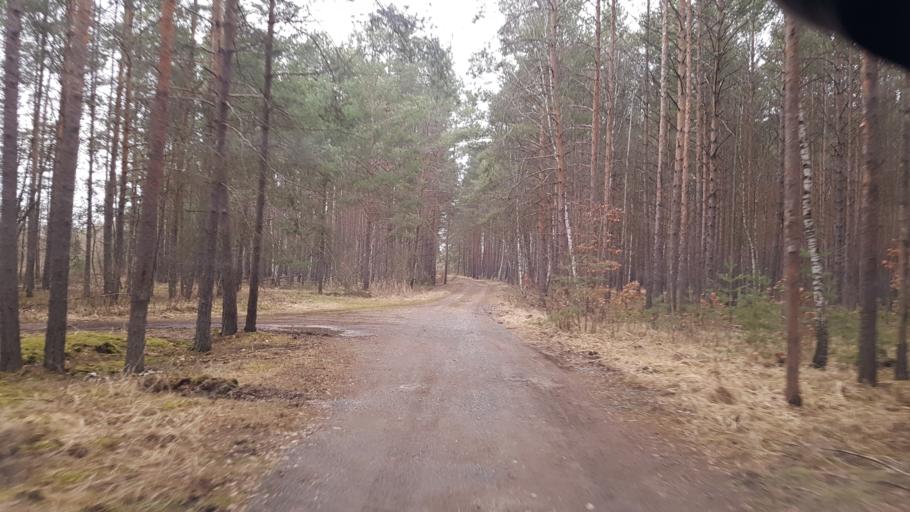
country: DE
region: Brandenburg
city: Trobitz
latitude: 51.6097
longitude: 13.4590
